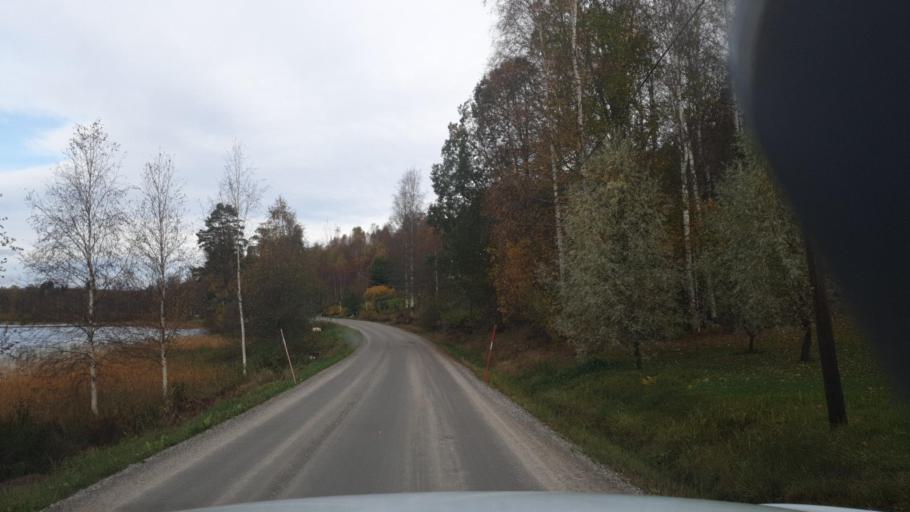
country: SE
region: Vaermland
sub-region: Arvika Kommun
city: Arvika
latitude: 59.7428
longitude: 12.8303
